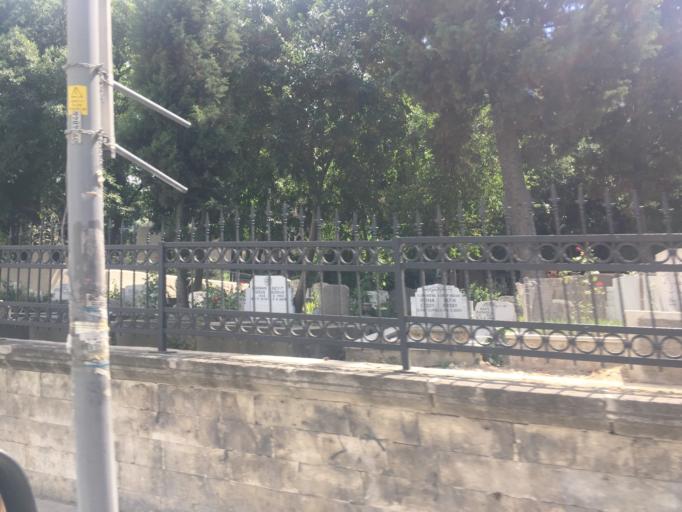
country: TR
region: Istanbul
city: Istanbul
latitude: 41.0262
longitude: 28.9194
